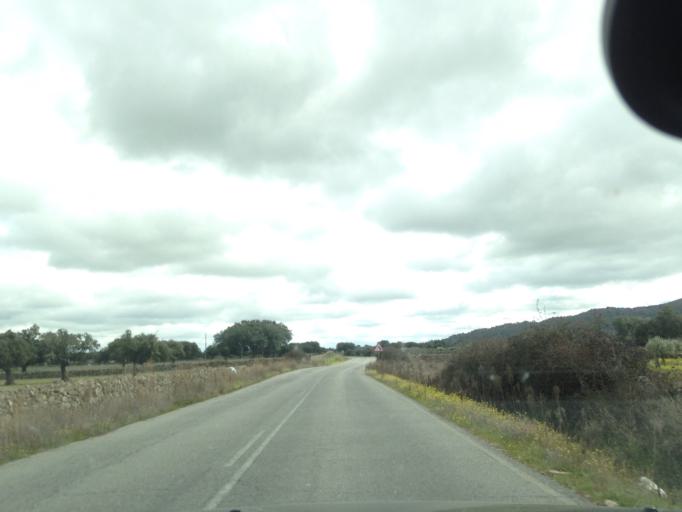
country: ES
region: Extremadura
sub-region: Provincia de Caceres
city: Albala
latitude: 39.2596
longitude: -6.1672
